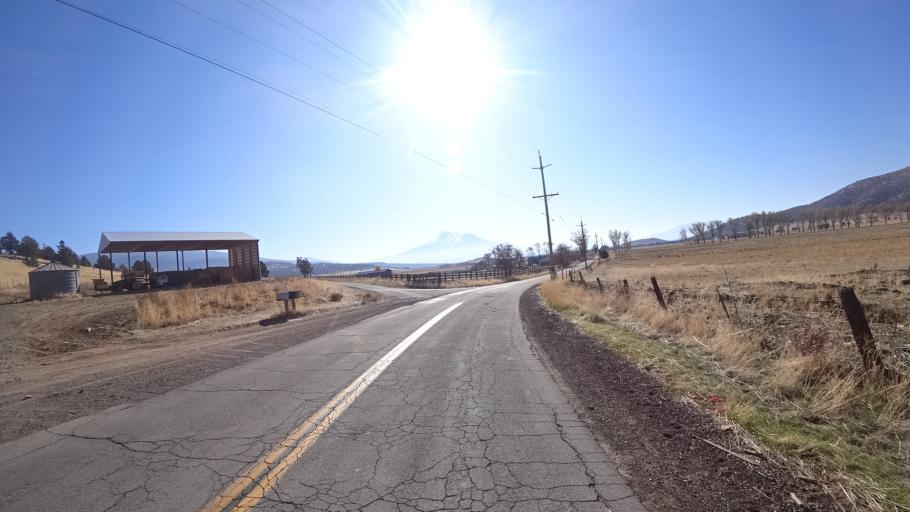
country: US
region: California
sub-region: Siskiyou County
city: Montague
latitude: 41.6891
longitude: -122.3699
